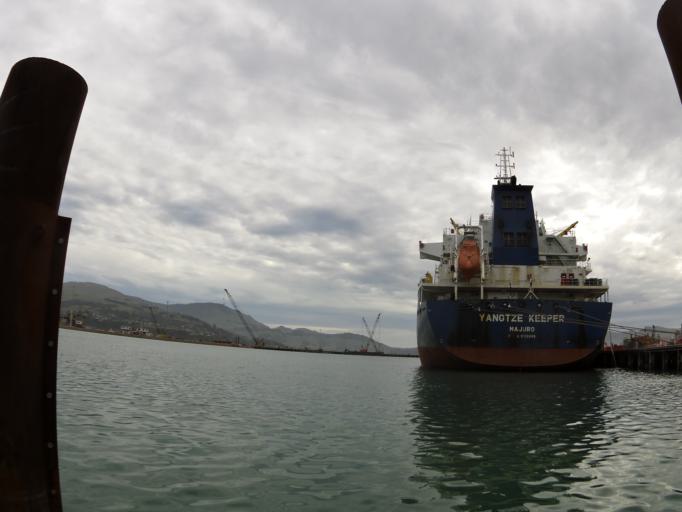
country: NZ
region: Canterbury
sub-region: Christchurch City
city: Christchurch
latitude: -43.6055
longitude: 172.7218
